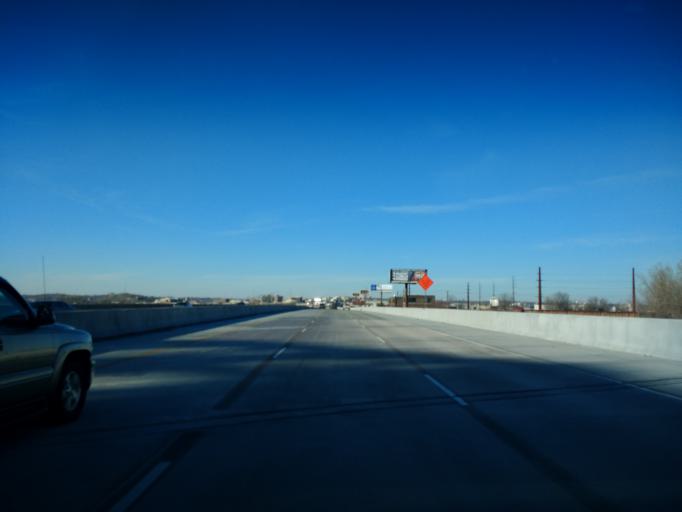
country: US
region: Iowa
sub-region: Woodbury County
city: Sioux City
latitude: 42.4756
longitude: -96.3840
